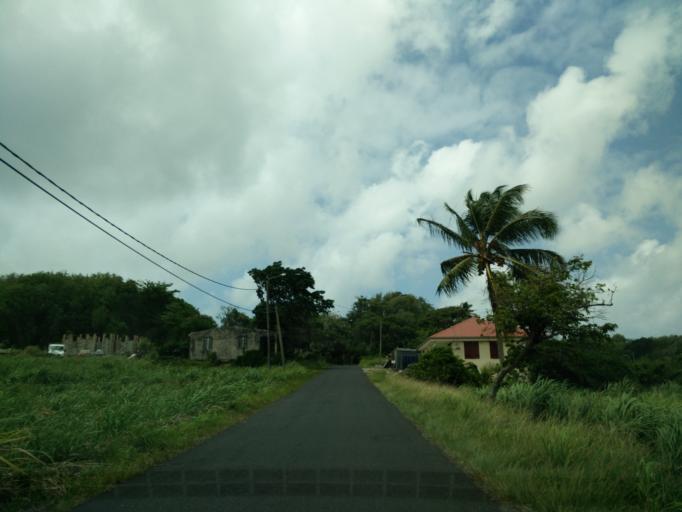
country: GP
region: Guadeloupe
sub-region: Guadeloupe
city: Grand-Bourg
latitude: 15.9140
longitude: -61.2742
